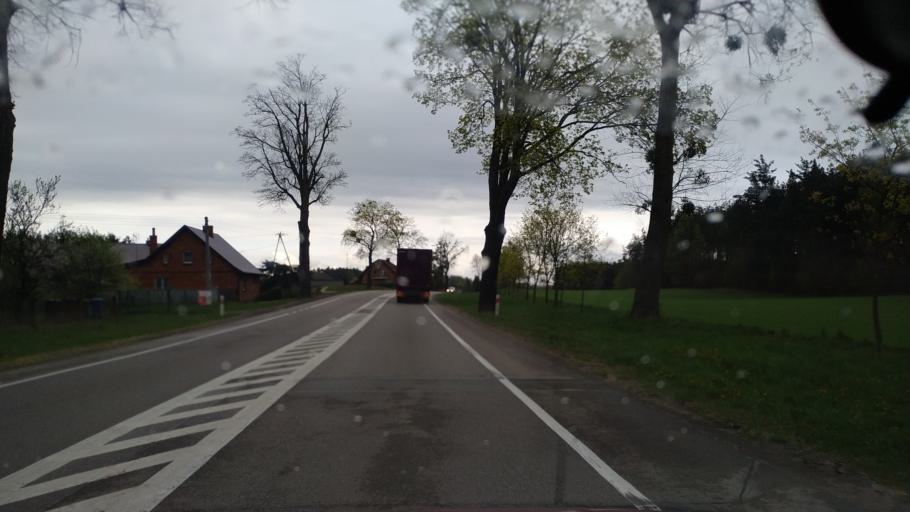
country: PL
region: Pomeranian Voivodeship
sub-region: Powiat starogardzki
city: Zblewo
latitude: 53.9239
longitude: 18.2871
